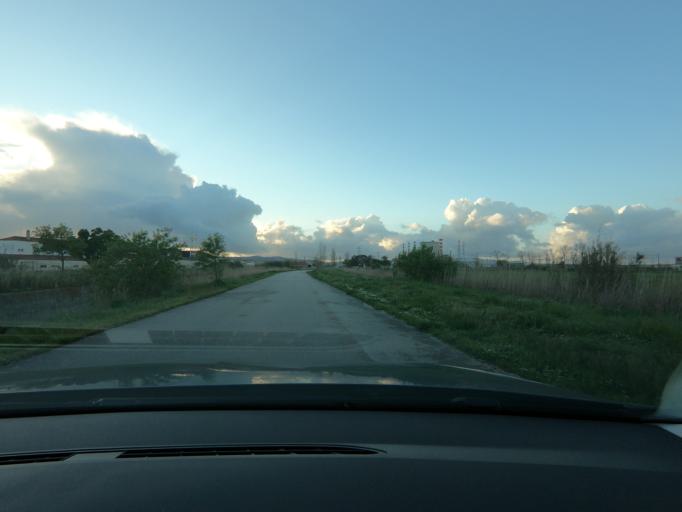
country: PT
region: Lisbon
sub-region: Vila Franca de Xira
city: Castanheira do Ribatejo
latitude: 39.0038
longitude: -8.9468
